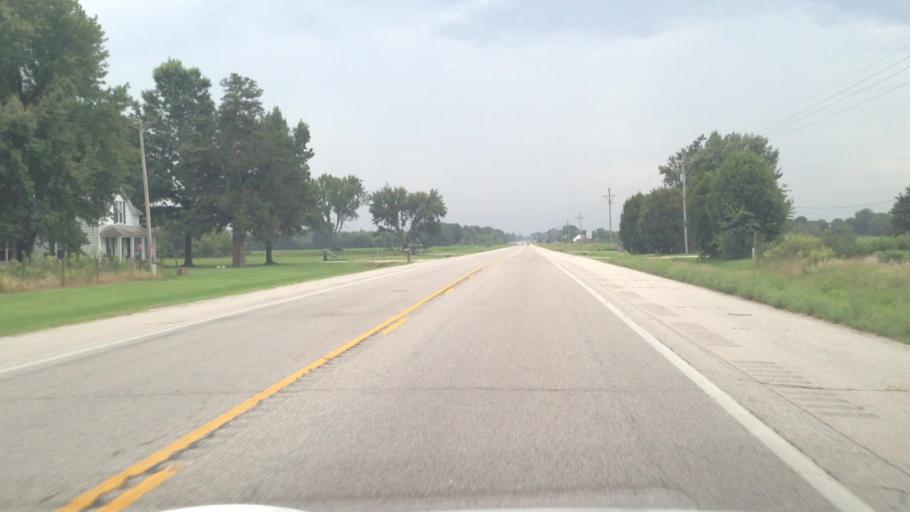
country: US
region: Kansas
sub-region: Cherokee County
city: Galena
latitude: 37.1023
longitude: -94.7045
